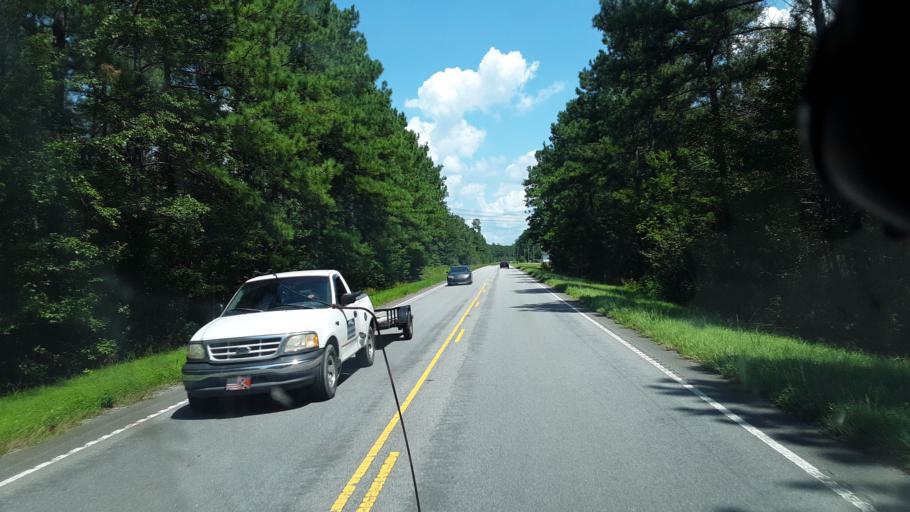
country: US
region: South Carolina
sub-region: Berkeley County
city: Bonneau Beach
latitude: 33.2591
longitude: -79.9311
